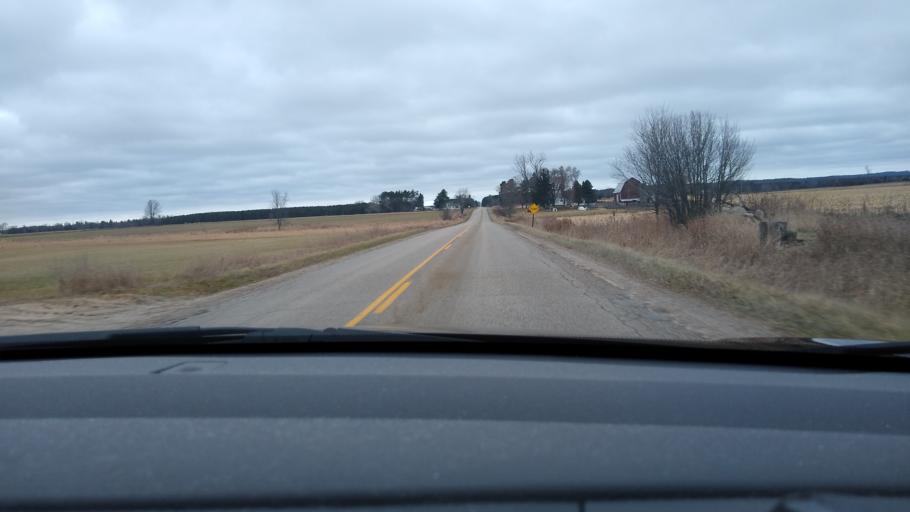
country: US
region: Michigan
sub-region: Missaukee County
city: Lake City
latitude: 44.2465
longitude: -85.0535
